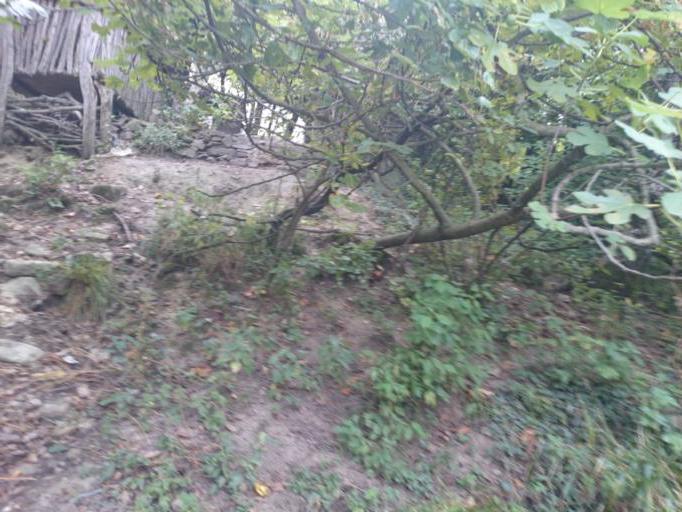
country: AL
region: Elbasan
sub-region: Rrethi i Elbasanit
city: Gjinar
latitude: 40.9763
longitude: 20.2076
